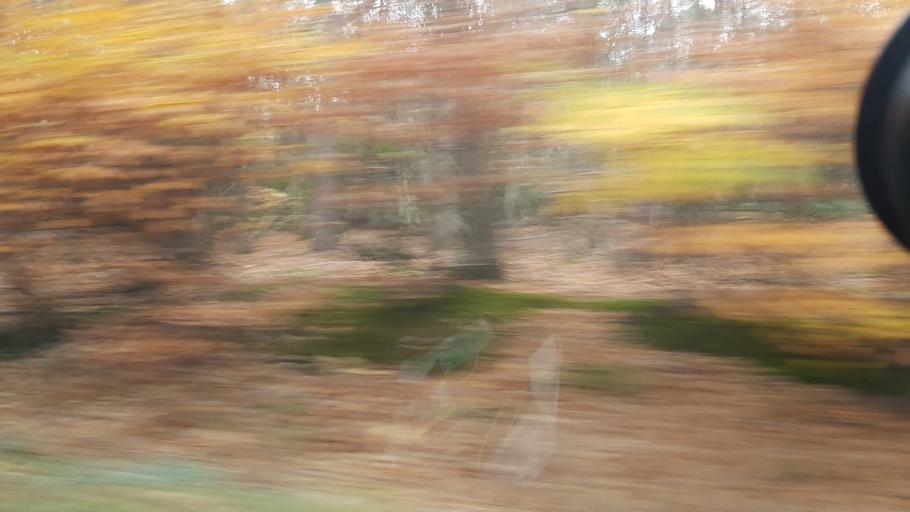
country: GB
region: England
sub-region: Hampshire
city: Fleet
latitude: 51.3080
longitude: -0.8061
